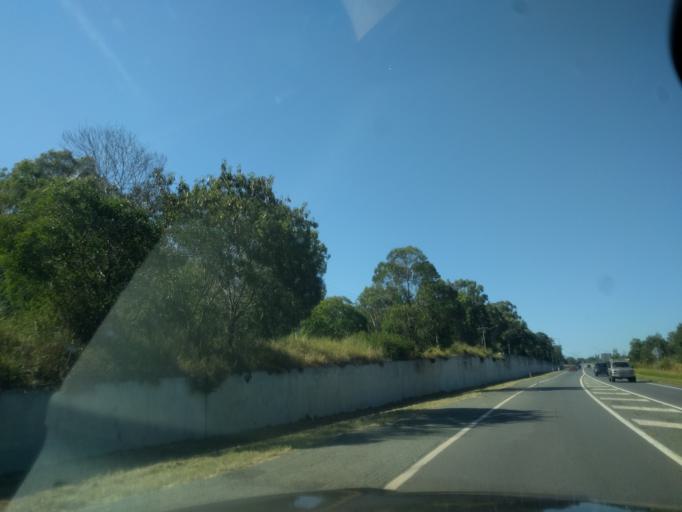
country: AU
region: Queensland
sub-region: Logan
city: Park Ridge South
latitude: -27.7218
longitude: 153.0311
